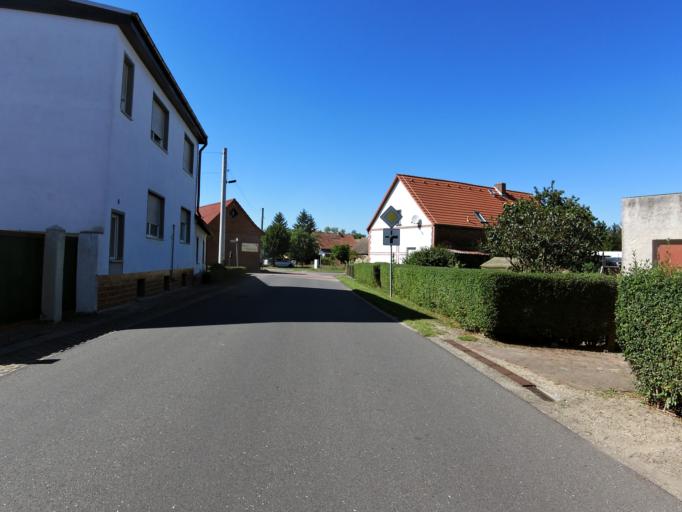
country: DE
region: Saxony-Anhalt
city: Muhlanger
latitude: 51.8456
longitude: 12.7448
